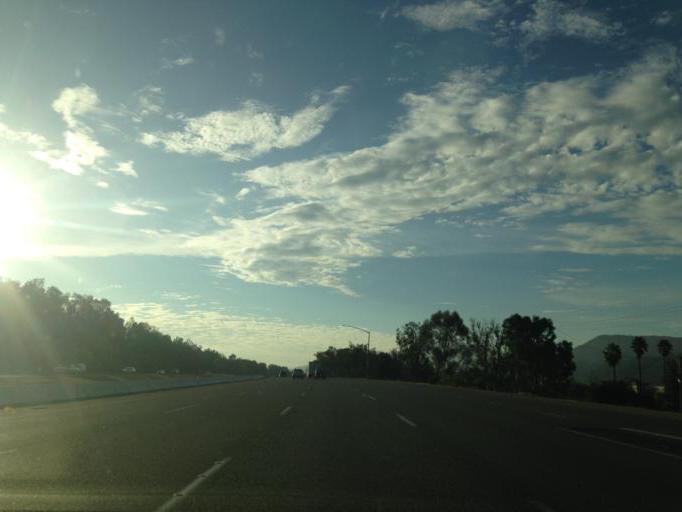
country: US
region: California
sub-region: Riverside County
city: Temecula
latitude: 33.4985
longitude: -117.1501
